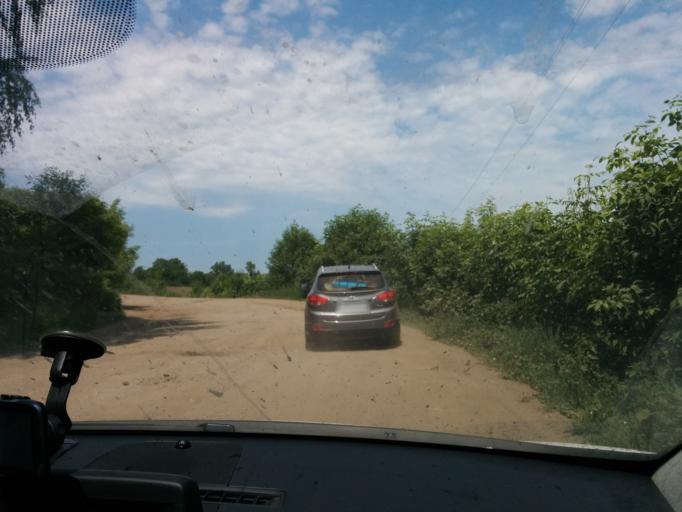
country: RU
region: Tambov
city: Morshansk
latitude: 53.6154
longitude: 41.8322
